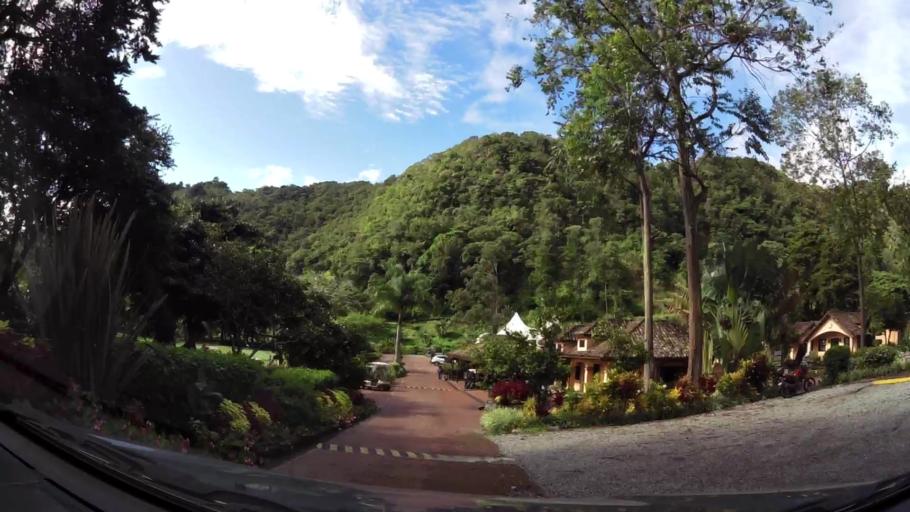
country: PA
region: Chiriqui
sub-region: Distrito Boquete
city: Boquete
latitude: 8.7813
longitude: -82.4412
